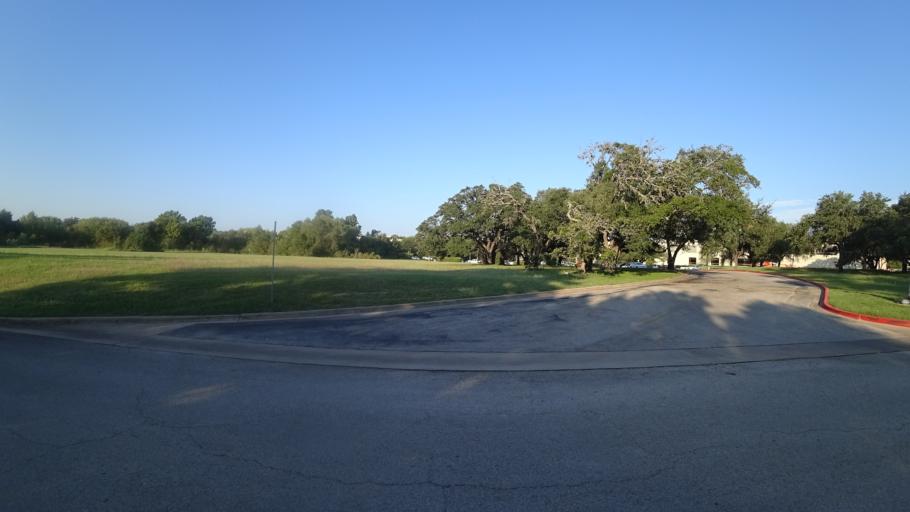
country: US
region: Texas
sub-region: Travis County
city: Austin
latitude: 30.3369
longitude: -97.6792
